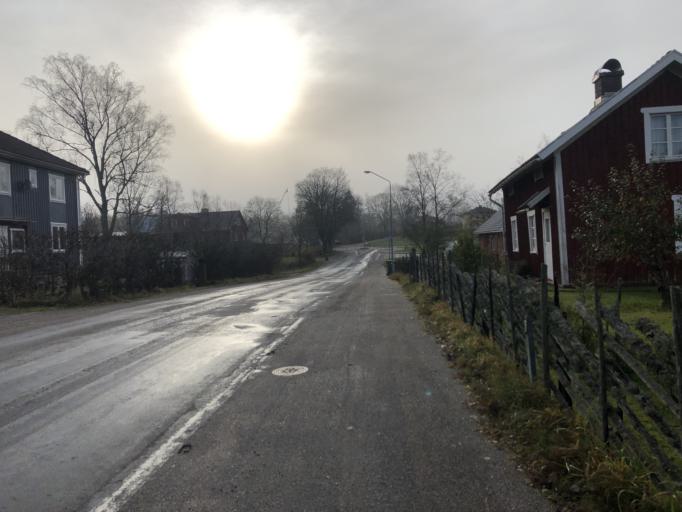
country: SE
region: Vaestra Goetaland
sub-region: Ulricehamns Kommun
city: Ulricehamn
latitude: 57.6954
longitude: 13.5726
